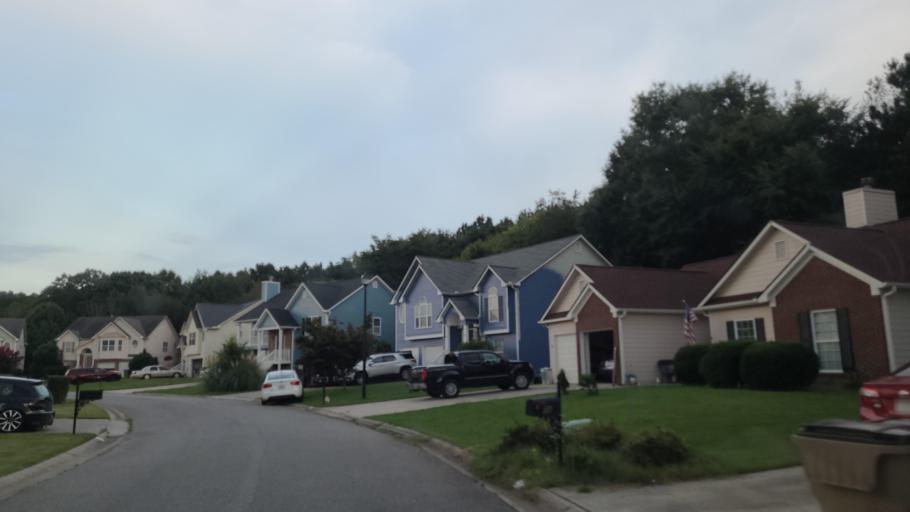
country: US
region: Georgia
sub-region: Bartow County
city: Cartersville
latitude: 34.2116
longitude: -84.7900
